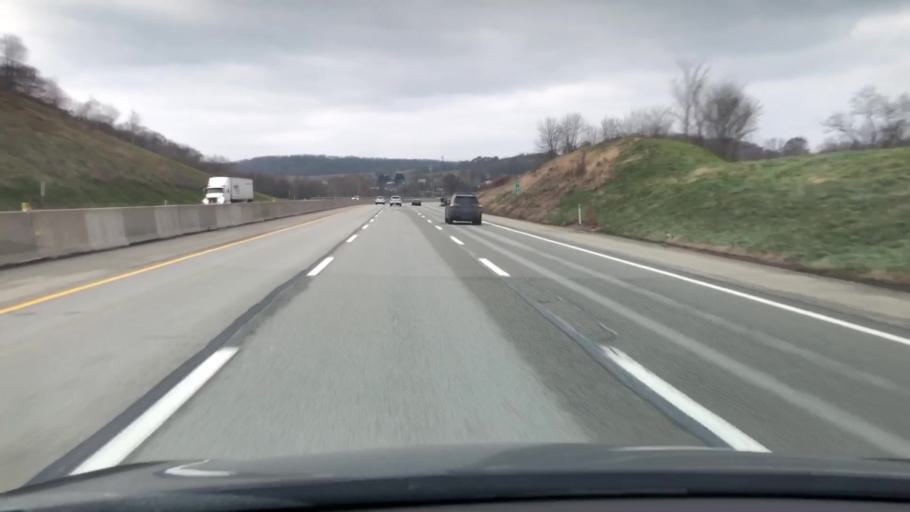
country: US
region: Pennsylvania
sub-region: Westmoreland County
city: New Stanton
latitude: 40.2651
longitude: -79.6611
